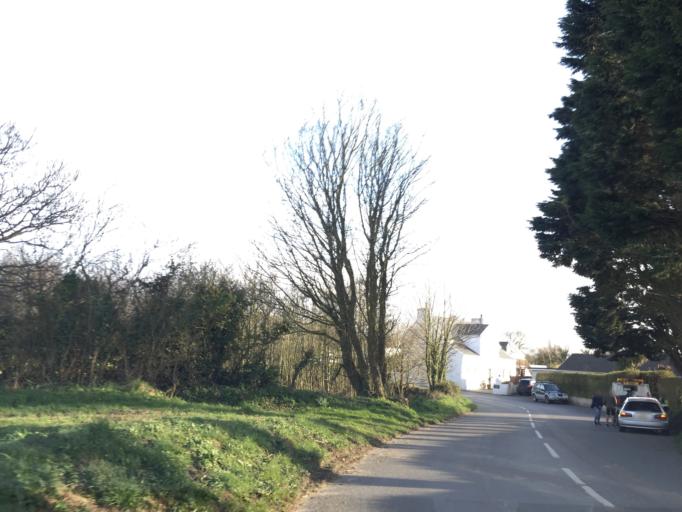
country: JE
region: St Helier
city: Saint Helier
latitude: 49.2453
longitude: -2.0984
